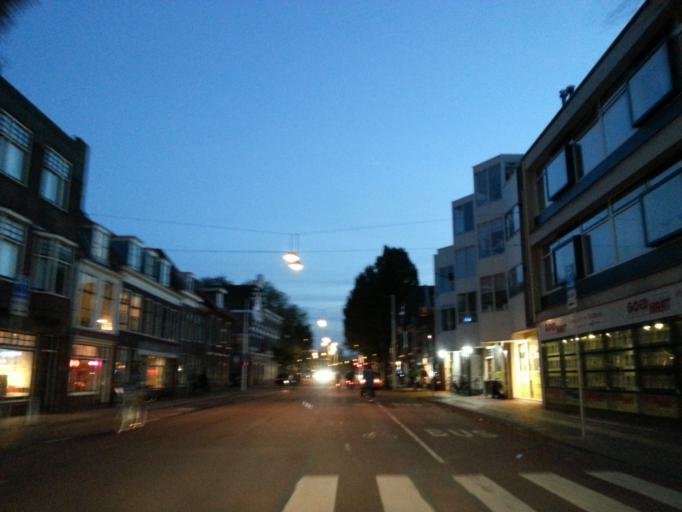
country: NL
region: South Holland
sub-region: Gemeente Leiden
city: Leiden
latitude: 52.1550
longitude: 4.4937
